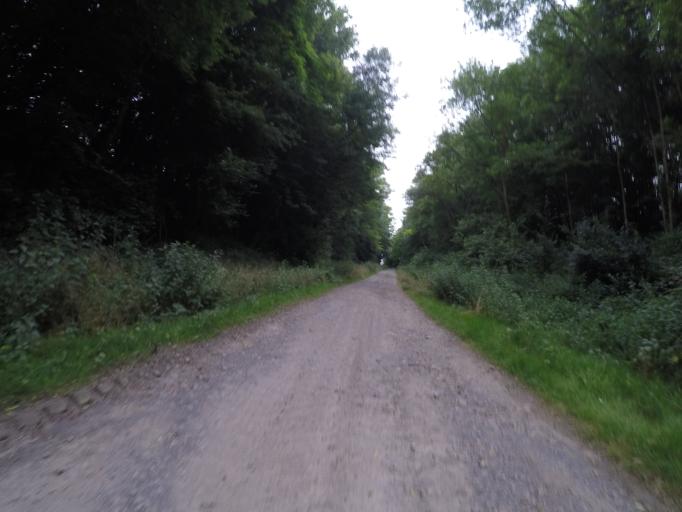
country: BE
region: Wallonia
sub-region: Province de Namur
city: Assesse
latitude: 50.2995
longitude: 5.0183
